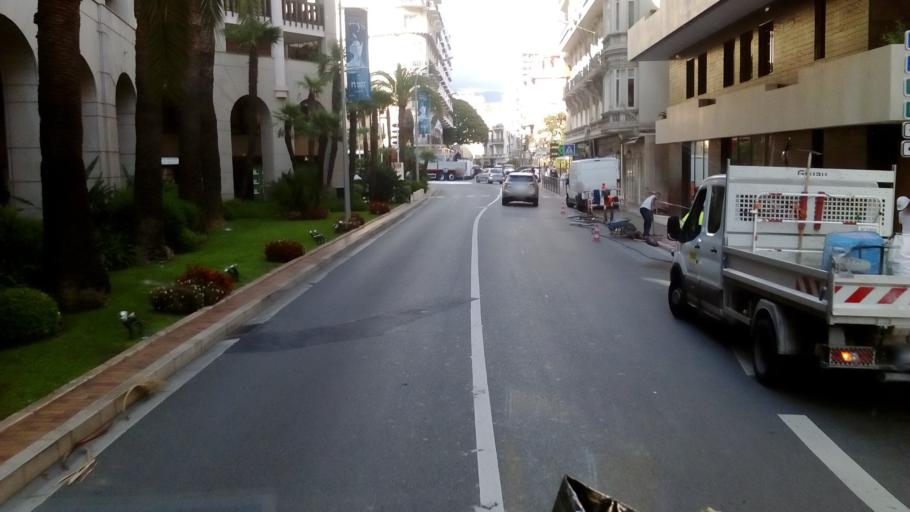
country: MC
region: Commune de Monaco
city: Monte-Carlo
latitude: 43.7411
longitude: 7.4261
